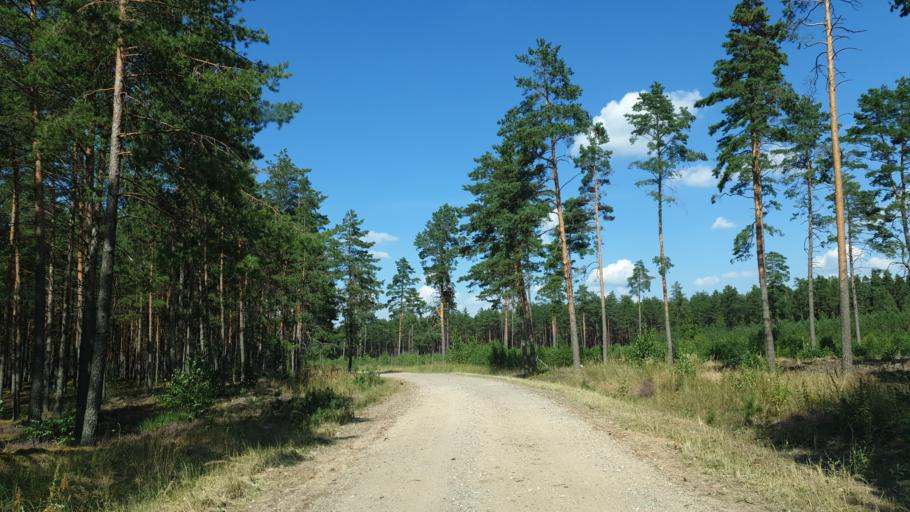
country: LT
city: Sirvintos
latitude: 54.9007
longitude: 24.9573
